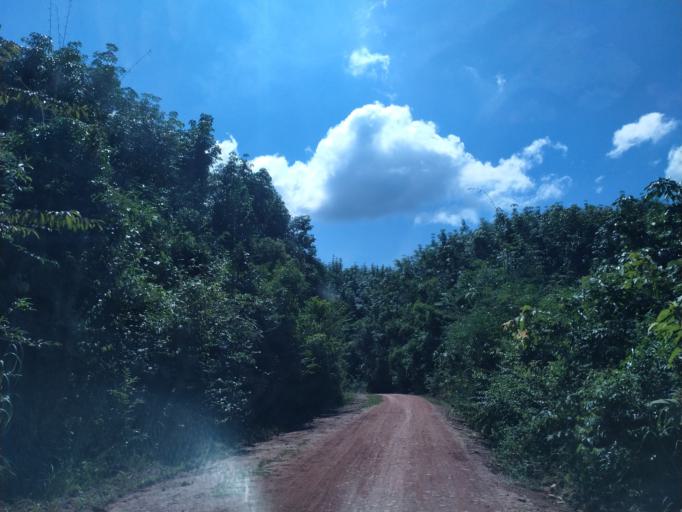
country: LA
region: Vientiane
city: Muang Phon-Hong
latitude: 18.6127
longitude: 102.8506
